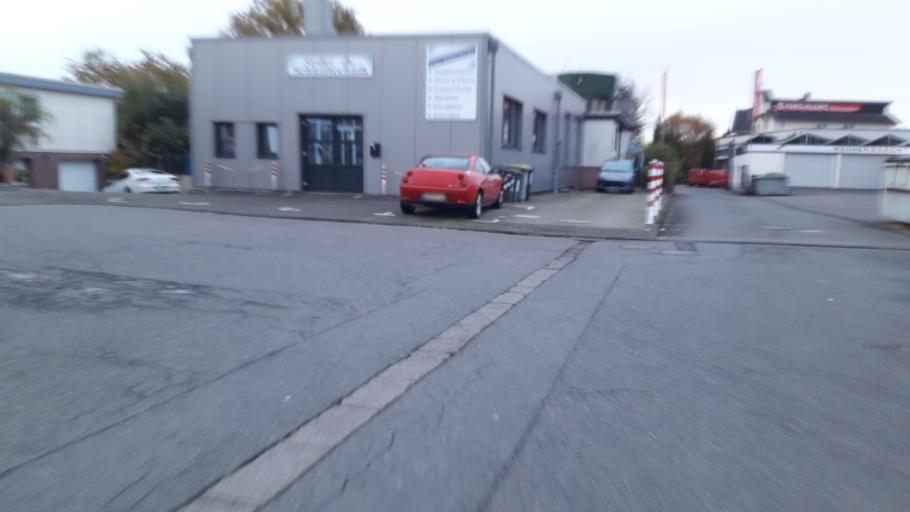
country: DE
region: North Rhine-Westphalia
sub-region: Regierungsbezirk Detmold
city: Paderborn
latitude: 51.7310
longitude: 8.7818
